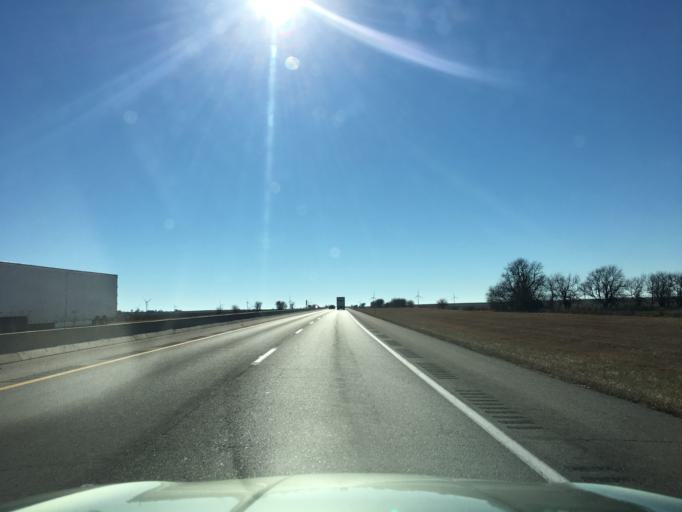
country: US
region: Kansas
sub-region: Sumner County
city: Wellington
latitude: 37.1828
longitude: -97.3396
